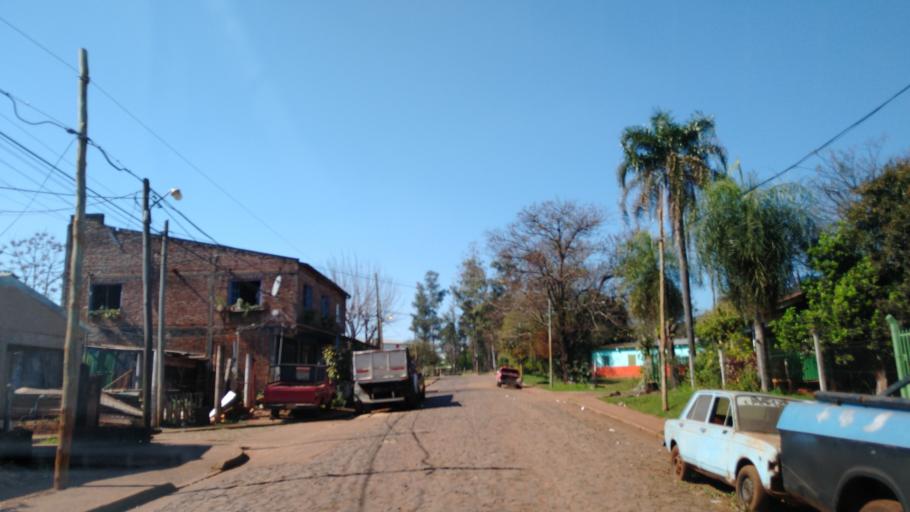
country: AR
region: Misiones
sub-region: Departamento de Capital
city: Posadas
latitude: -27.4181
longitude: -55.9583
